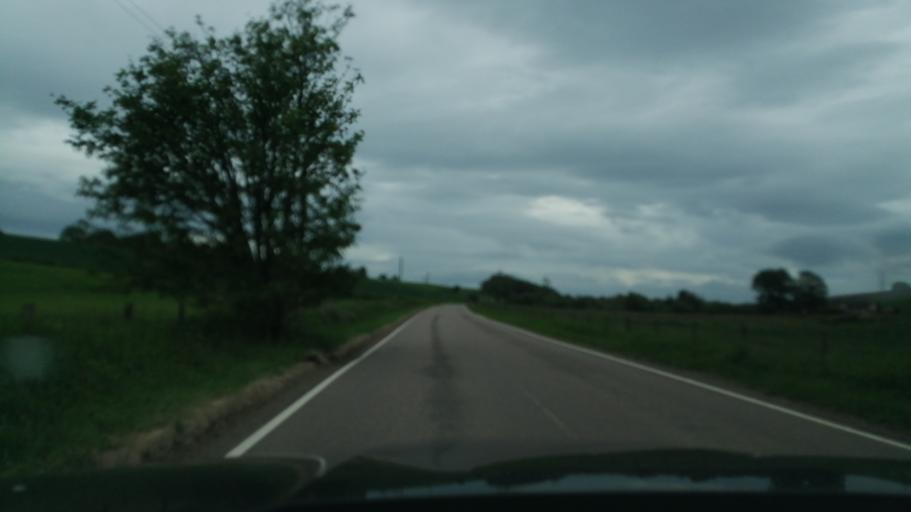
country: GB
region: Scotland
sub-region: Moray
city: Cullen
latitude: 57.6058
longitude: -2.8528
